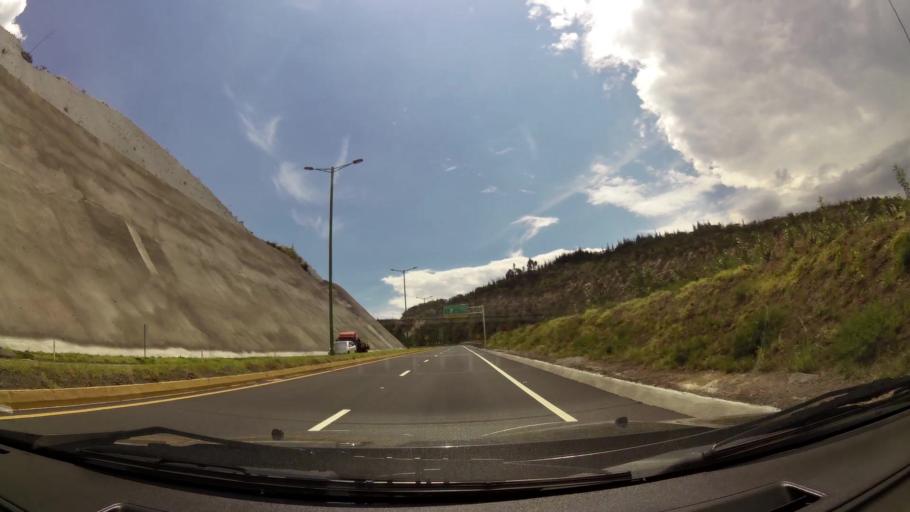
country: EC
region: Pichincha
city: Quito
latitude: -0.0953
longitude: -78.3910
